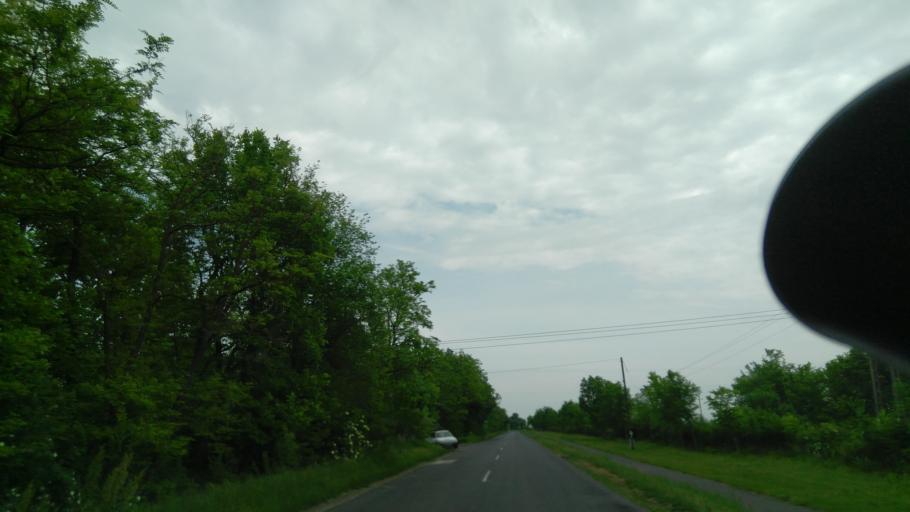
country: HU
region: Bekes
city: Szeghalom
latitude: 47.0485
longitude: 21.1904
